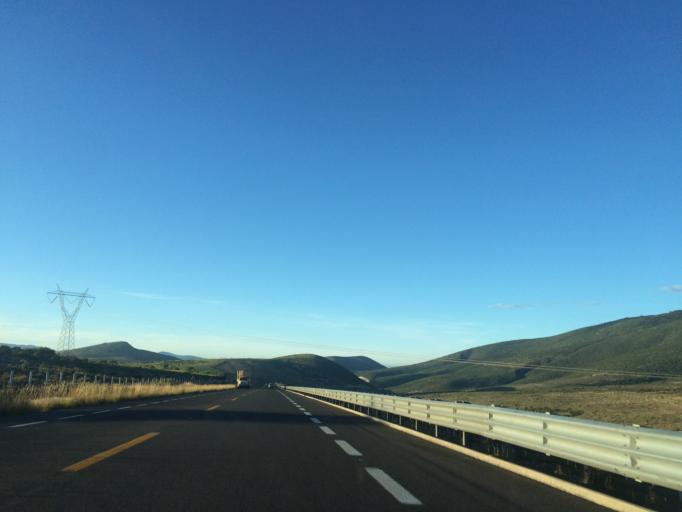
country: MX
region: Puebla
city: Morelos Canada
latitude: 18.6956
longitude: -97.4639
